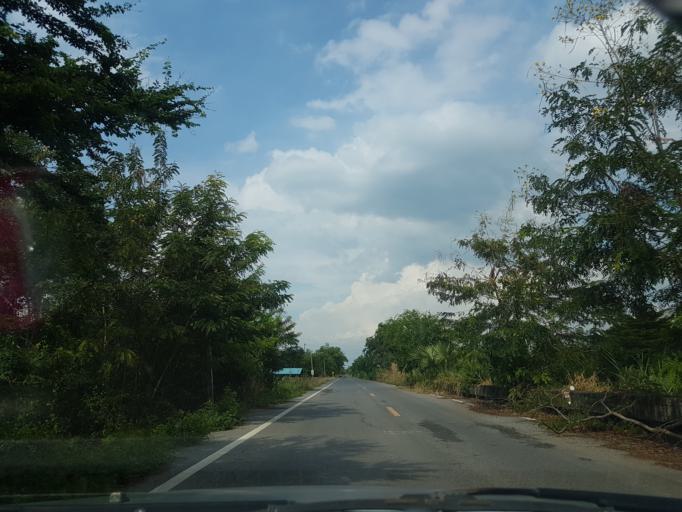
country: TH
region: Sara Buri
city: Nong Khae
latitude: 14.2288
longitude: 100.8914
